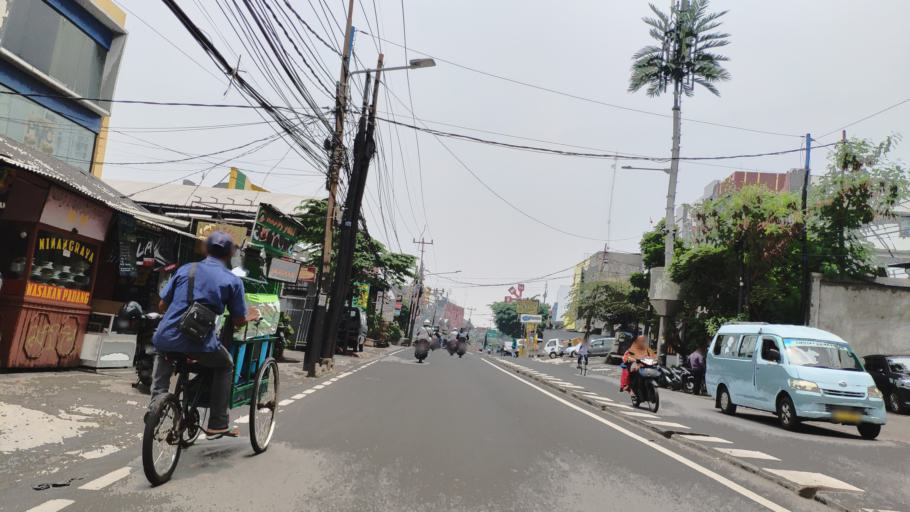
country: ID
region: Banten
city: South Tangerang
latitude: -6.2587
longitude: 106.7775
